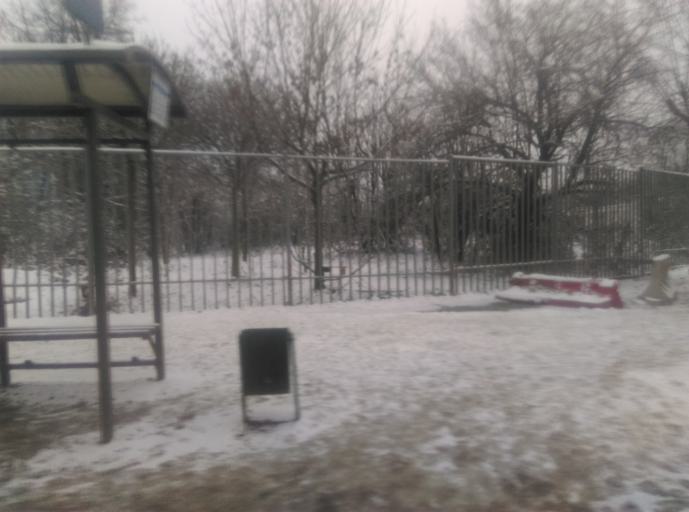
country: RU
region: Moscow
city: Mikhalkovo
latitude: 55.6983
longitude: 37.4232
